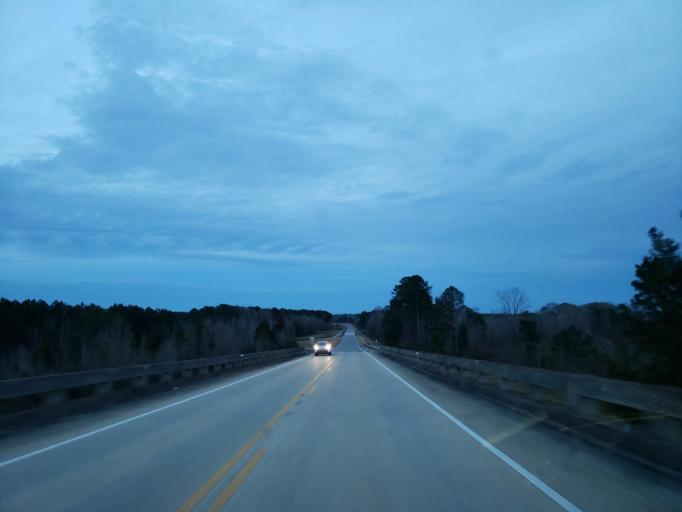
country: US
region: Alabama
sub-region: Greene County
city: Eutaw
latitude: 32.8406
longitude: -88.1347
